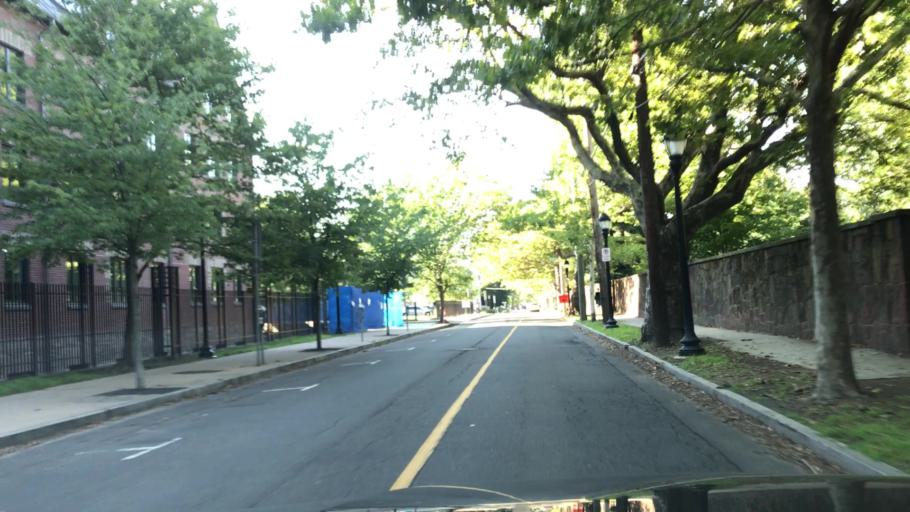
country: US
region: Connecticut
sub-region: New Haven County
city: New Haven
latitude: 41.3136
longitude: -72.9285
